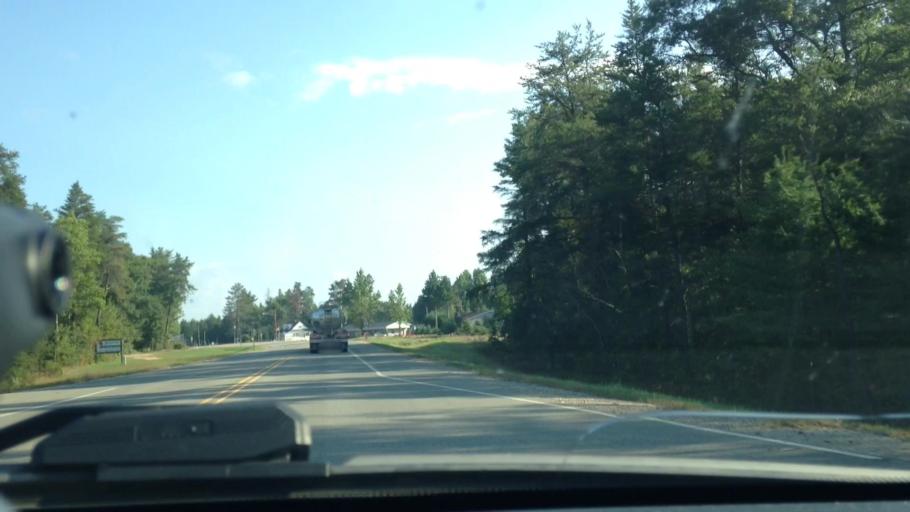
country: US
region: Wisconsin
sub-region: Marinette County
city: Niagara
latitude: 45.5868
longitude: -87.9959
